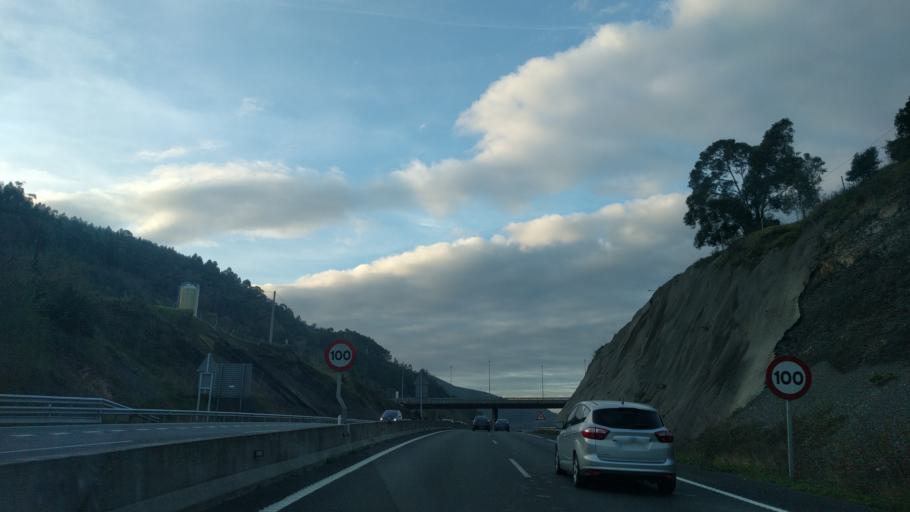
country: ES
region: Basque Country
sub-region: Bizkaia
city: San Julian de Muskiz
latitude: 43.3421
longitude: -3.1542
